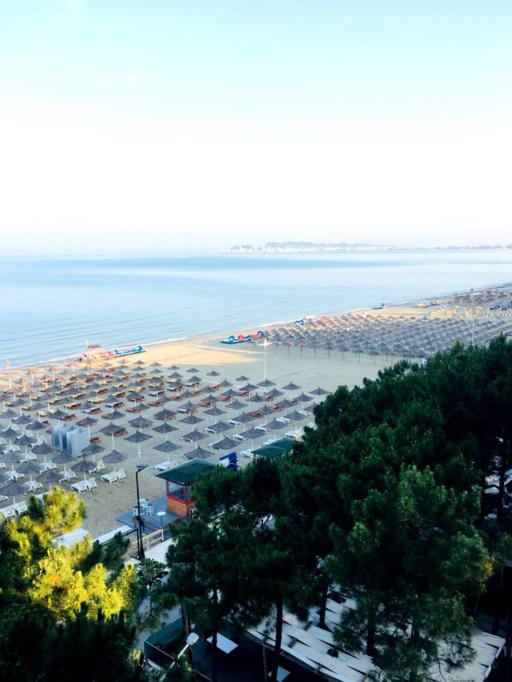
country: AL
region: Tirane
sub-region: Rrethi i Kavajes
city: Golem
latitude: 41.2681
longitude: 19.5190
